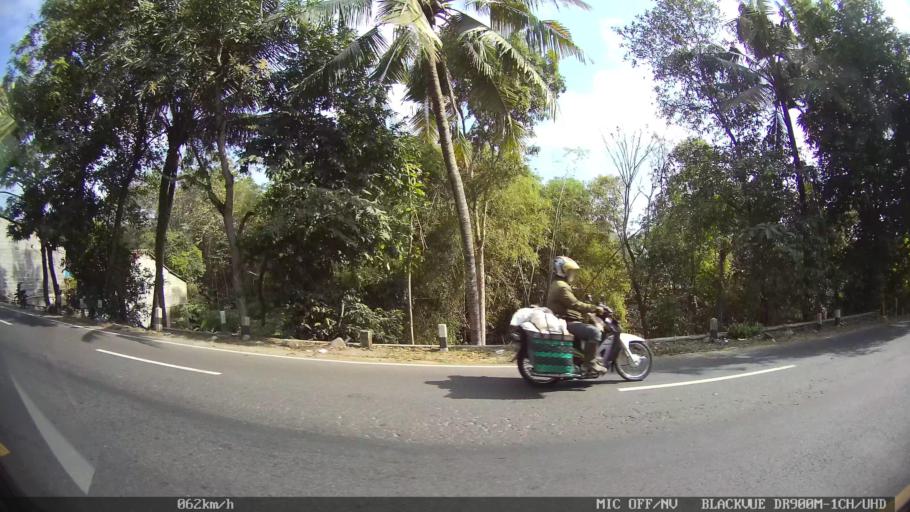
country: ID
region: Daerah Istimewa Yogyakarta
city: Godean
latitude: -7.8156
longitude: 110.2514
